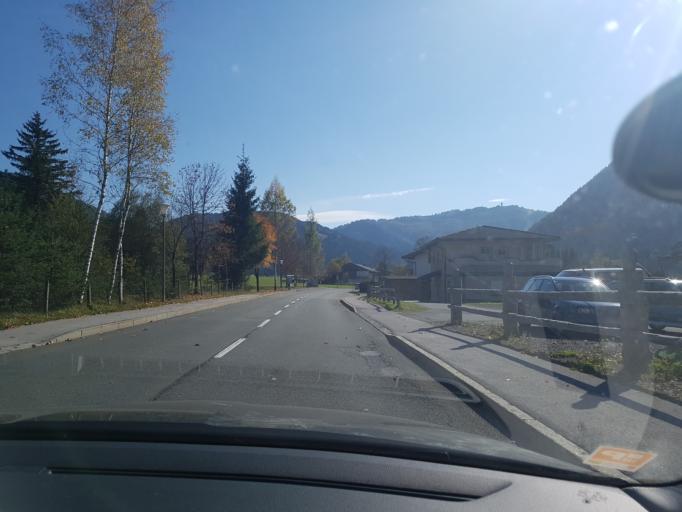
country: AT
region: Tyrol
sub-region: Politischer Bezirk Kitzbuhel
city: Fieberbrunn
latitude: 47.5232
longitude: 12.5775
